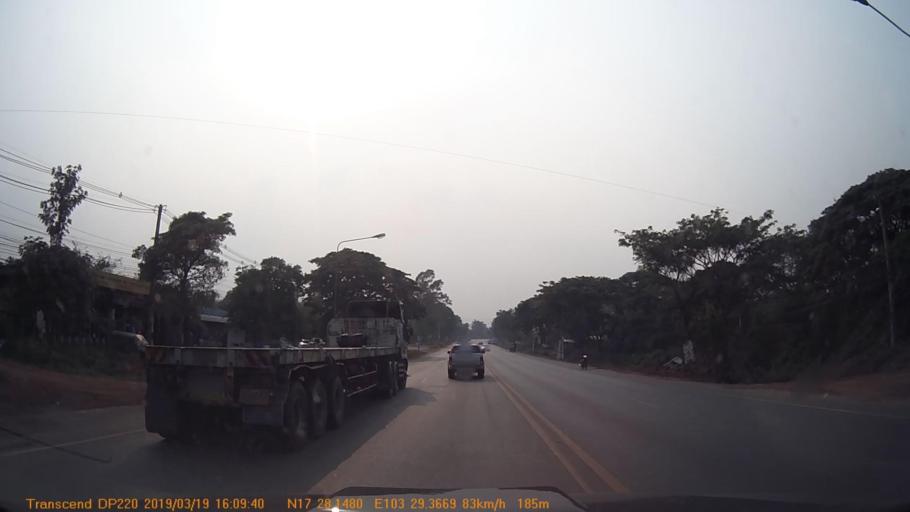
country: TH
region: Sakon Nakhon
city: Sawang Daen Din
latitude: 17.4692
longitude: 103.4890
